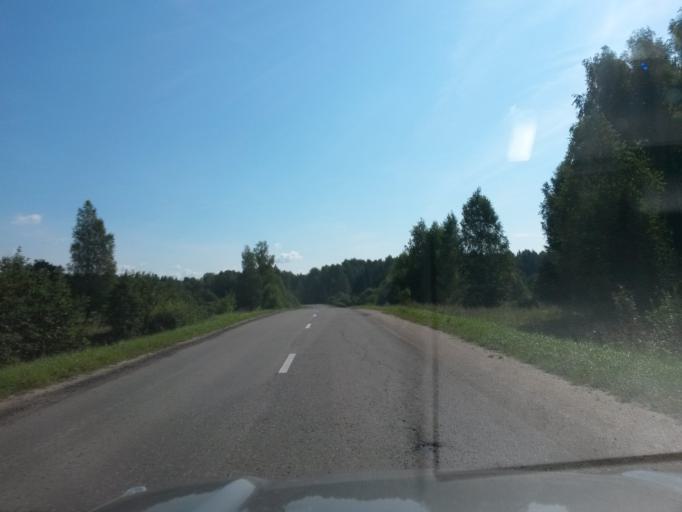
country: RU
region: Jaroslavl
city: Gavrilov-Yam
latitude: 57.3019
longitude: 40.0032
